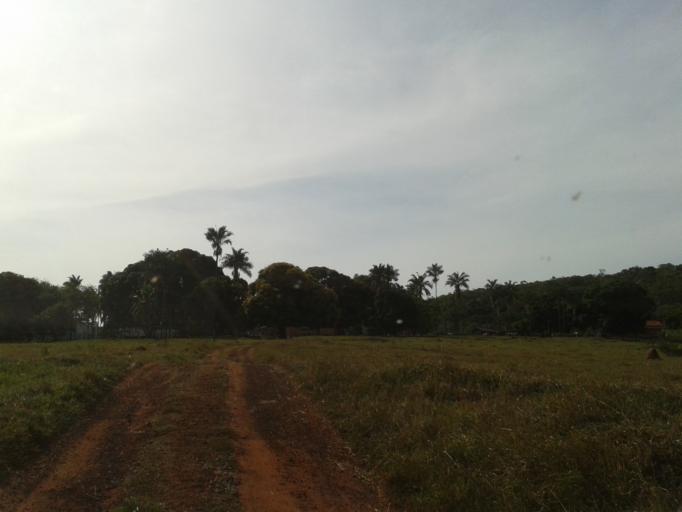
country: BR
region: Minas Gerais
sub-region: Campina Verde
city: Campina Verde
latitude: -19.4945
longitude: -49.5760
